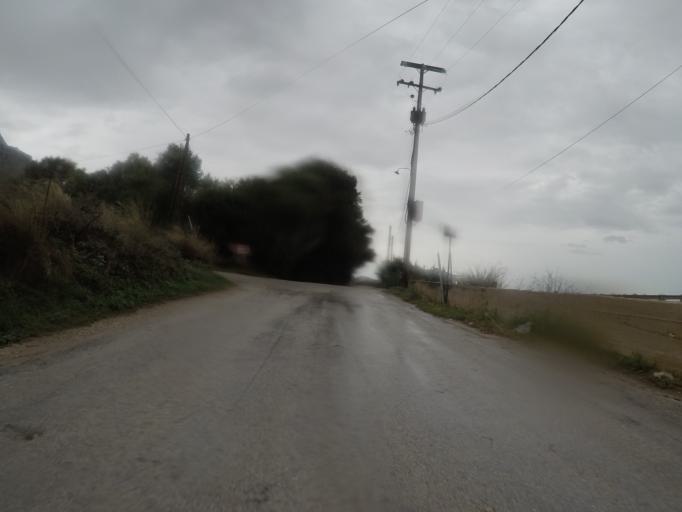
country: GR
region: Peloponnese
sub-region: Nomos Korinthias
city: Arkhaia Korinthos
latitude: 37.9017
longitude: 22.8835
